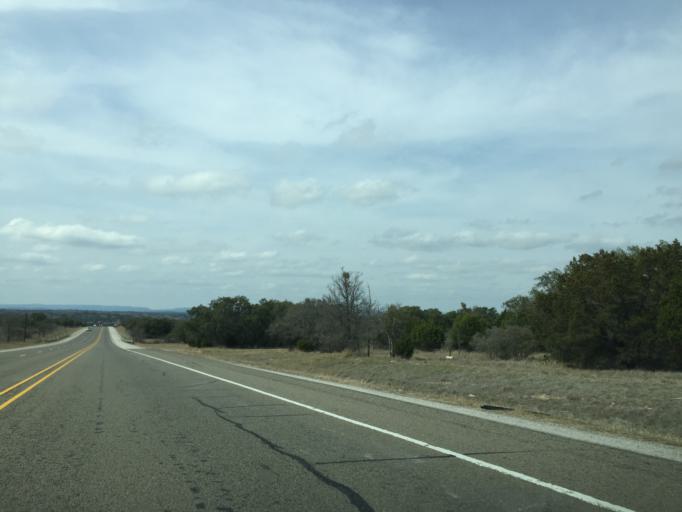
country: US
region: Texas
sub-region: Llano County
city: Horseshoe Bay
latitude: 30.5138
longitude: -98.3867
